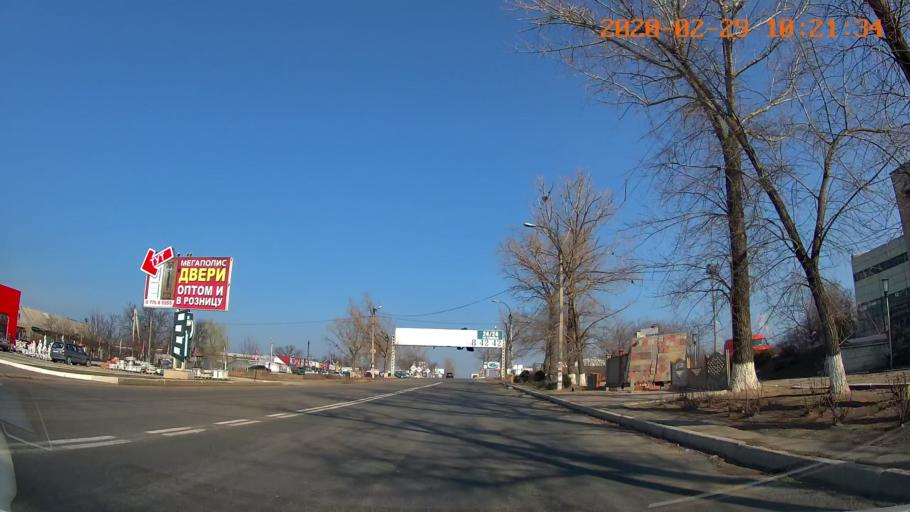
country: MD
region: Telenesti
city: Tiraspolul Nou
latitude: 46.8676
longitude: 29.6091
